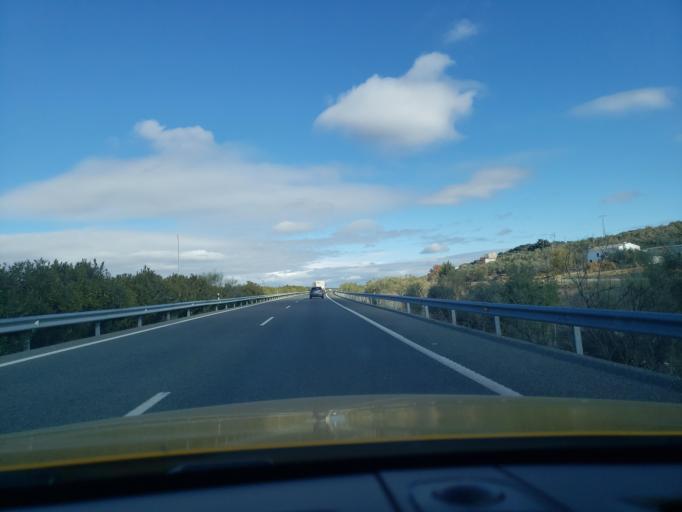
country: ES
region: Andalusia
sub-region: Provincia de Malaga
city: Archidona
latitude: 37.1043
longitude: -4.3125
